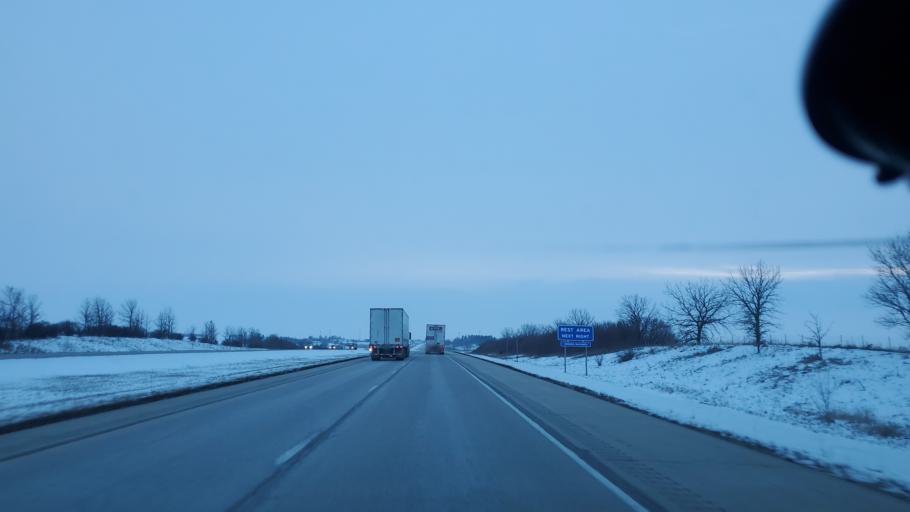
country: US
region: Illinois
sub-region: LaSalle County
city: Earlville
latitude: 41.7390
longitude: -89.0093
